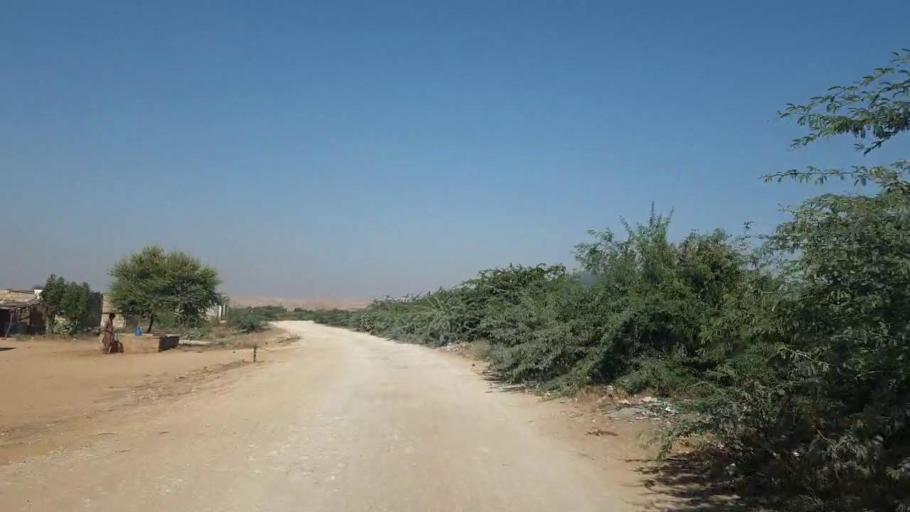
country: PK
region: Sindh
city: Gharo
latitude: 25.1695
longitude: 67.7337
